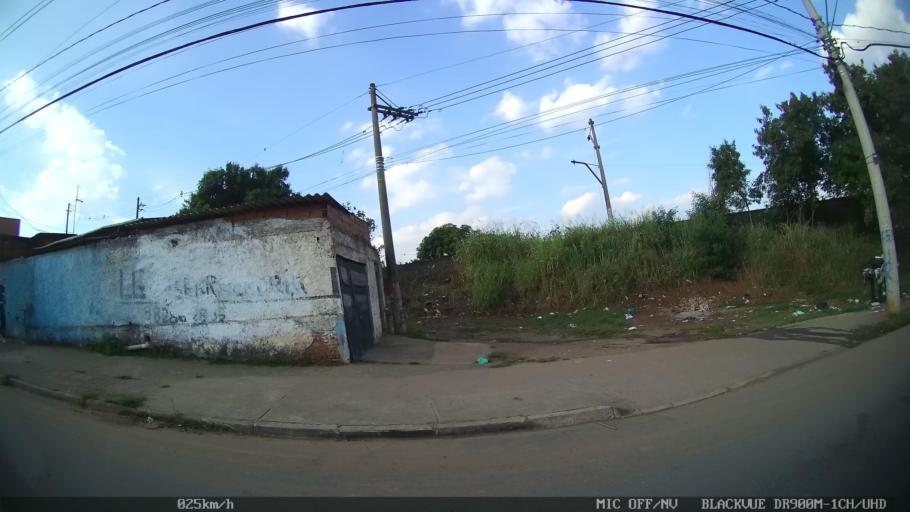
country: BR
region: Sao Paulo
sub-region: Hortolandia
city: Hortolandia
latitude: -22.8664
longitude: -47.1424
